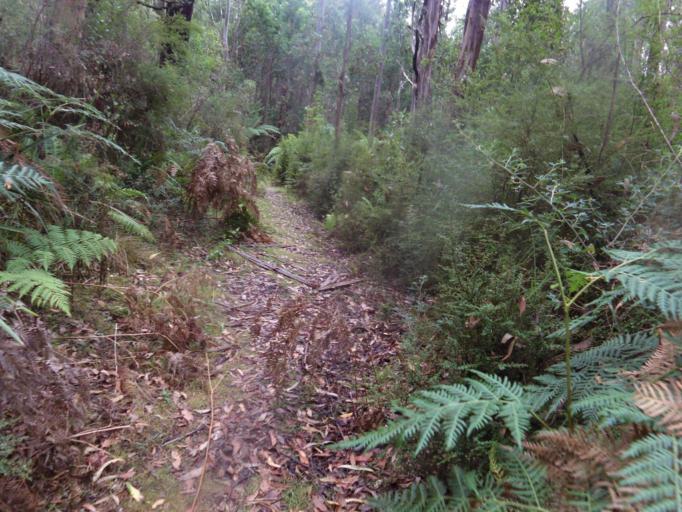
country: AU
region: Victoria
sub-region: Nillumbik
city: Saint Andrews
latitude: -37.5372
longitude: 145.3504
